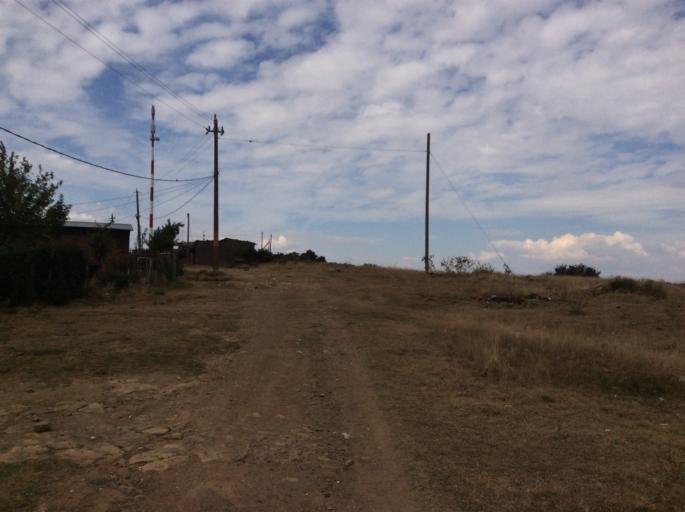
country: LS
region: Mafeteng
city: Mafeteng
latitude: -29.7223
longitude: 27.0291
